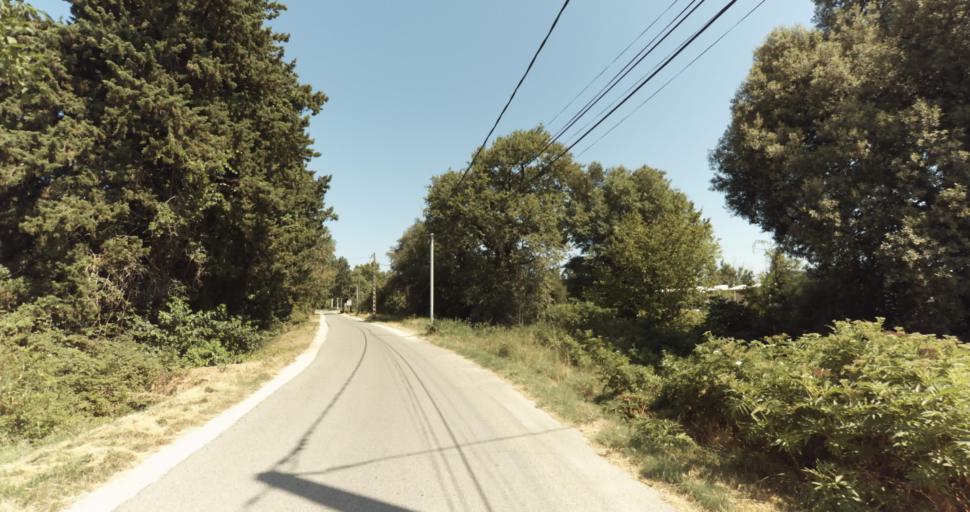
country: FR
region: Provence-Alpes-Cote d'Azur
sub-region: Departement du Vaucluse
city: Althen-des-Paluds
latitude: 44.0207
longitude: 4.9763
